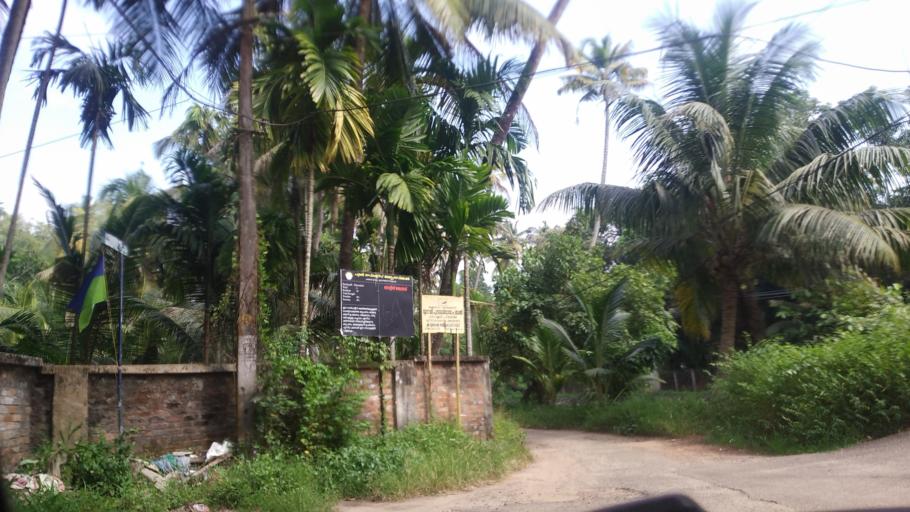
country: IN
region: Kerala
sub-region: Ernakulam
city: Elur
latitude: 10.0897
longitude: 76.2092
